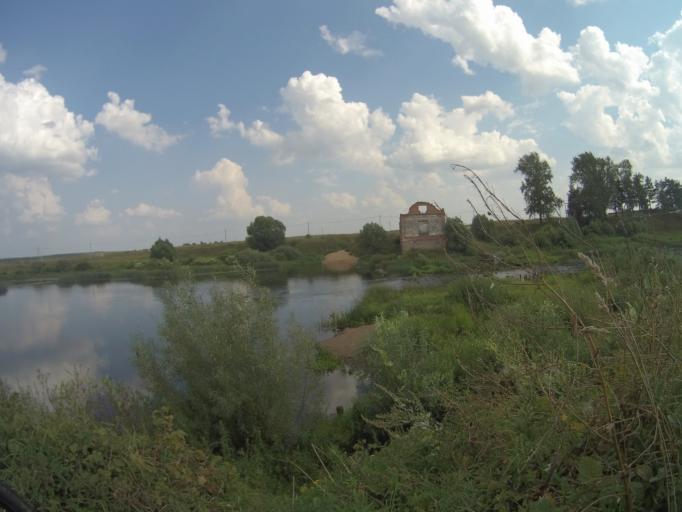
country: RU
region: Vladimir
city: Kideksha
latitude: 56.3316
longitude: 40.5951
